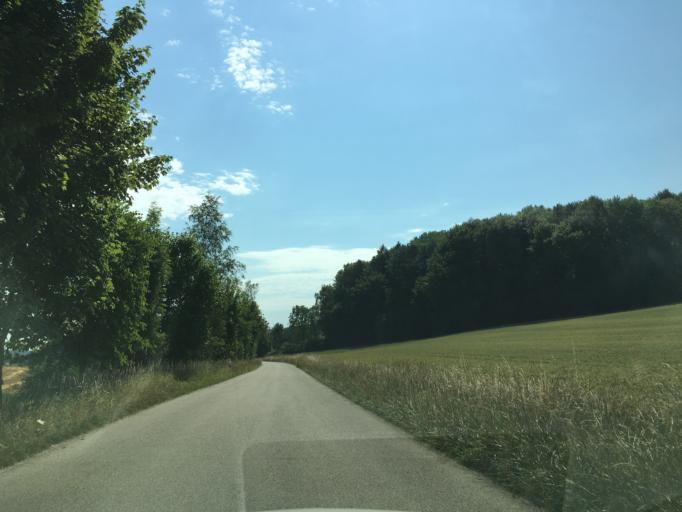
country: DE
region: Bavaria
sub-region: Upper Bavaria
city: Steinhoring
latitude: 48.1162
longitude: 12.0622
